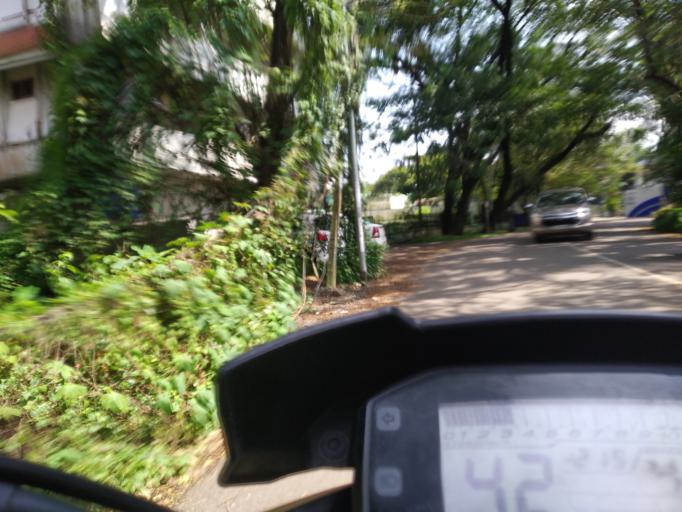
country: IN
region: Kerala
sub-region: Ernakulam
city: Cochin
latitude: 9.9692
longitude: 76.2936
